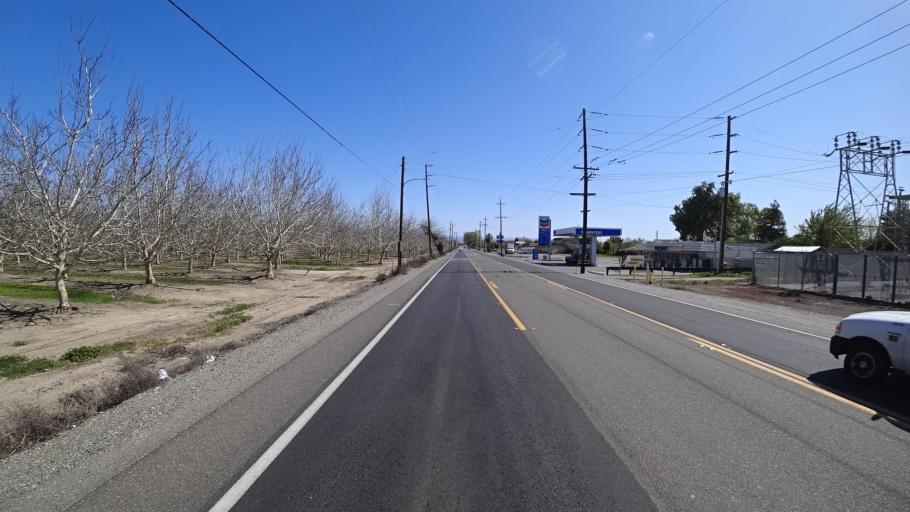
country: US
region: California
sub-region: Glenn County
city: Hamilton City
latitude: 39.7467
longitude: -122.0117
